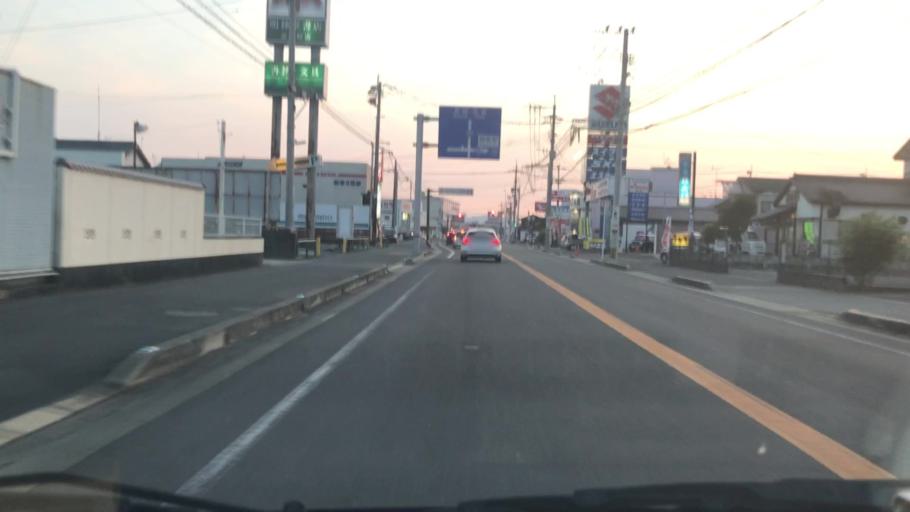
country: JP
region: Saga Prefecture
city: Saga-shi
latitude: 33.2447
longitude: 130.2679
